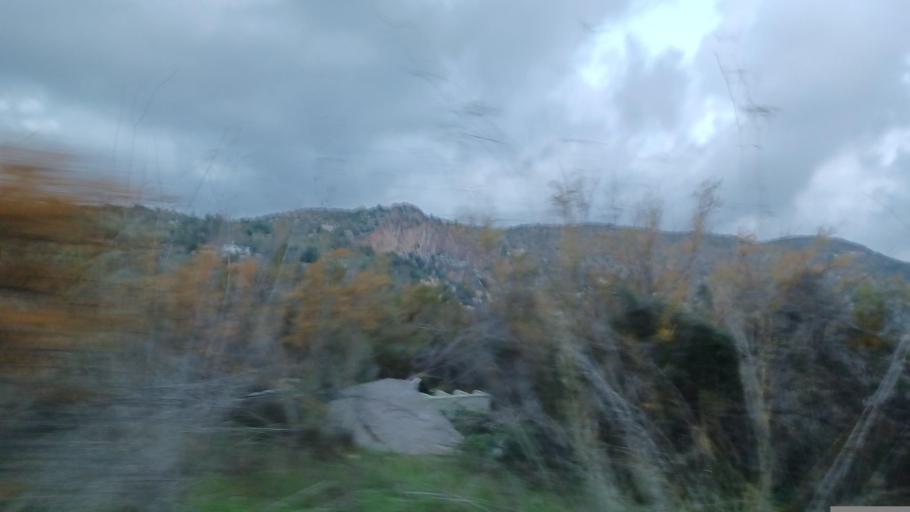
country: CY
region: Pafos
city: Mesogi
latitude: 34.7926
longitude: 32.5324
